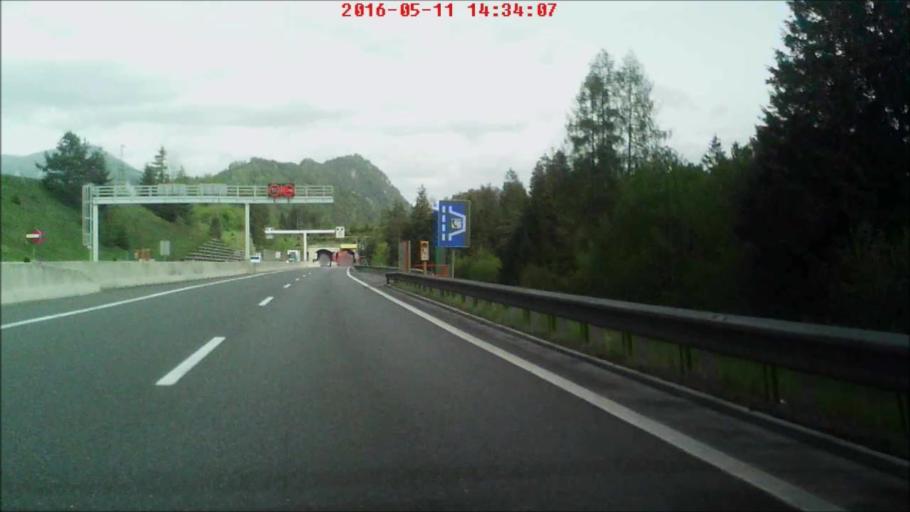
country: AT
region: Upper Austria
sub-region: Politischer Bezirk Kirchdorf an der Krems
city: Rossleithen
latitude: 47.7512
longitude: 14.2457
